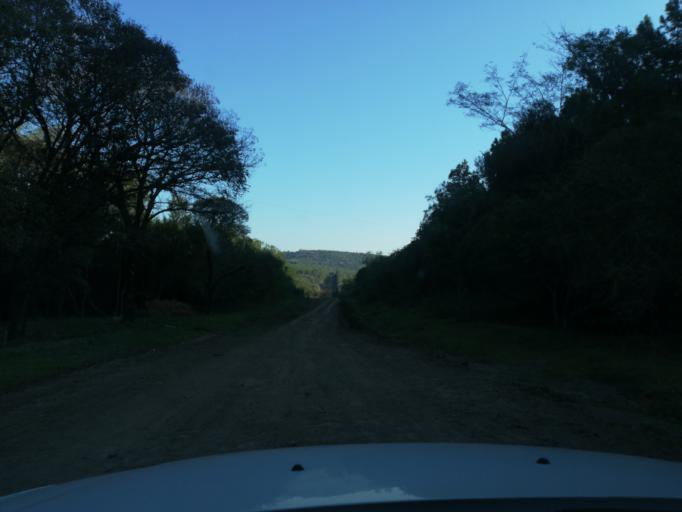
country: AR
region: Misiones
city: Cerro Cora
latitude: -27.5966
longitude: -55.6964
